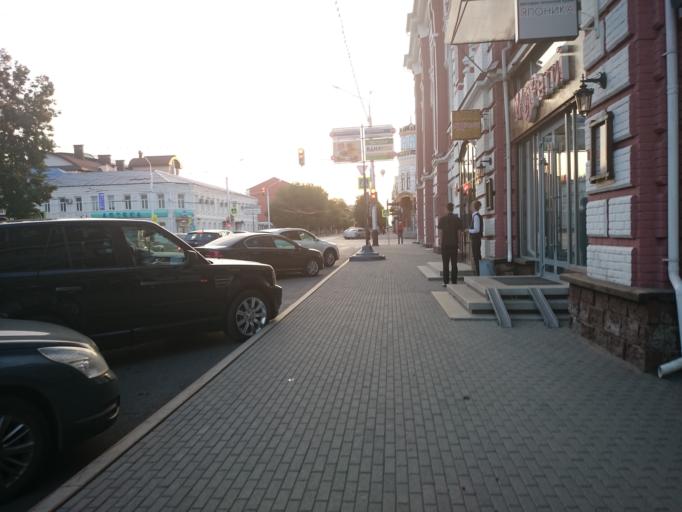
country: RU
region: Bashkortostan
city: Ufa
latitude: 54.7270
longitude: 55.9423
